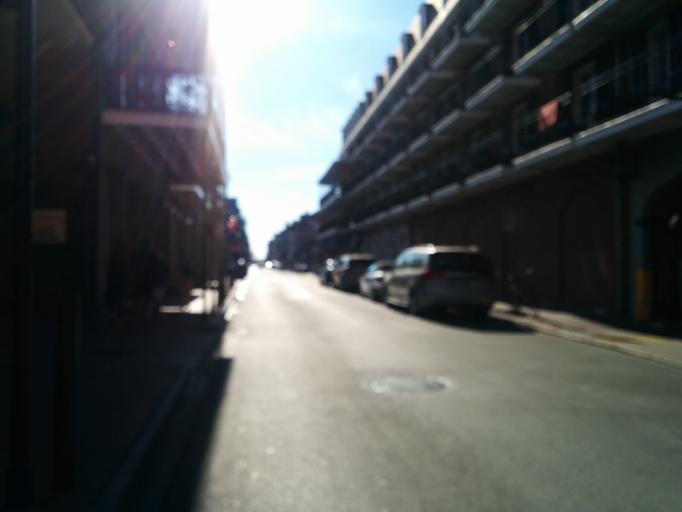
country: US
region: Louisiana
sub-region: Orleans Parish
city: New Orleans
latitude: 29.9582
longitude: -90.0670
